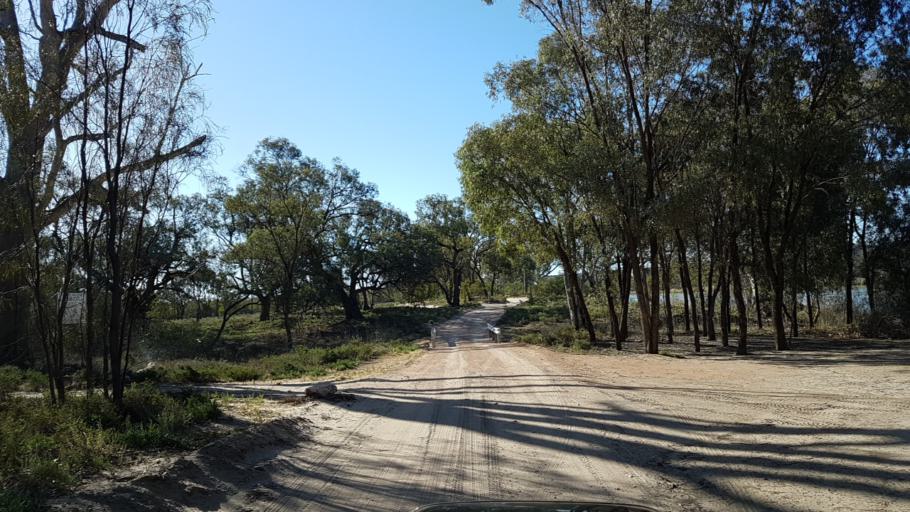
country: AU
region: South Australia
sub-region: Loxton Waikerie
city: Waikerie
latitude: -34.1613
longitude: 140.0317
